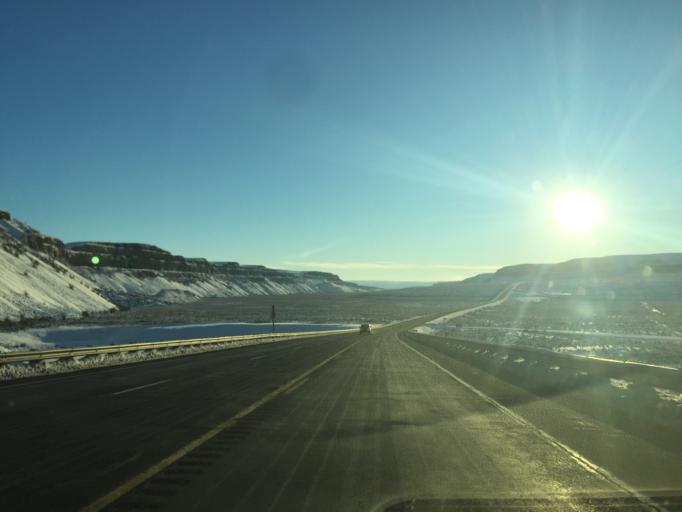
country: US
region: Washington
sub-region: Grant County
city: Soap Lake
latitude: 47.6021
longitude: -119.6679
